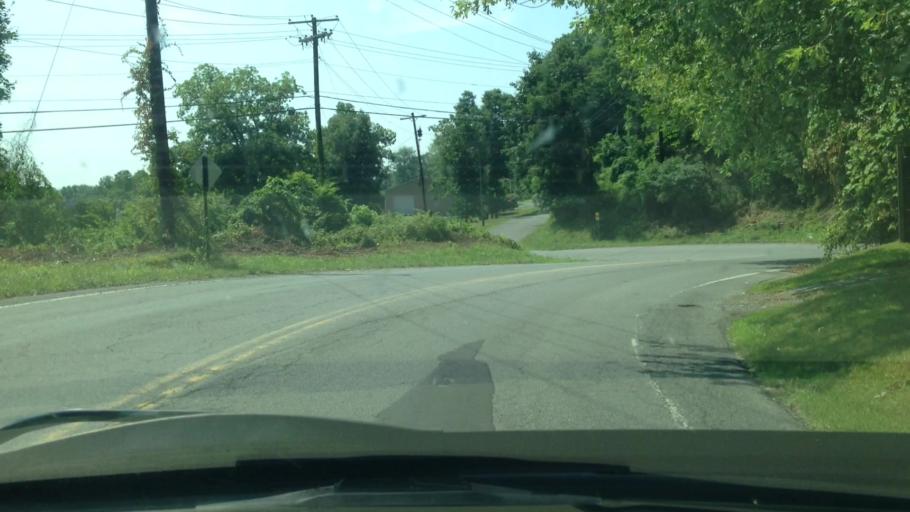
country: US
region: New York
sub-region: Ulster County
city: Port Ewen
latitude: 41.8995
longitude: -73.9894
